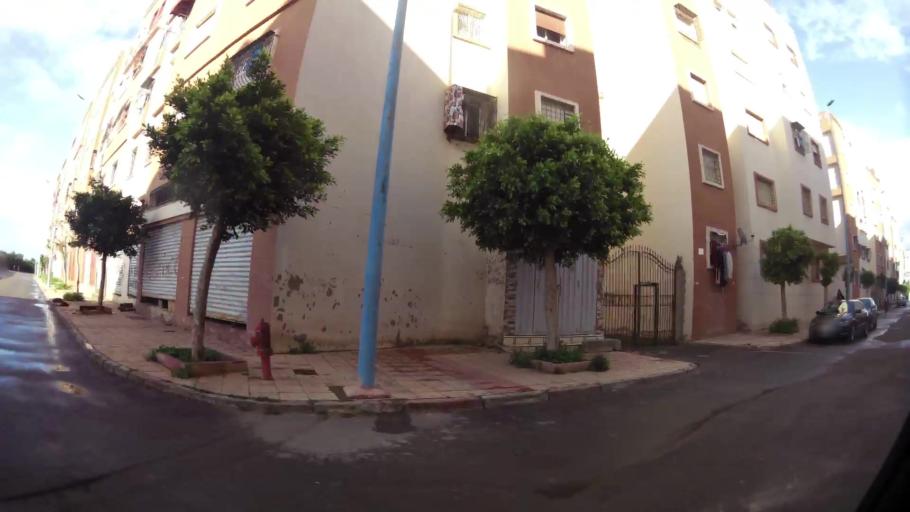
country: MA
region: Grand Casablanca
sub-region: Casablanca
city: Casablanca
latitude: 33.5558
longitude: -7.7055
